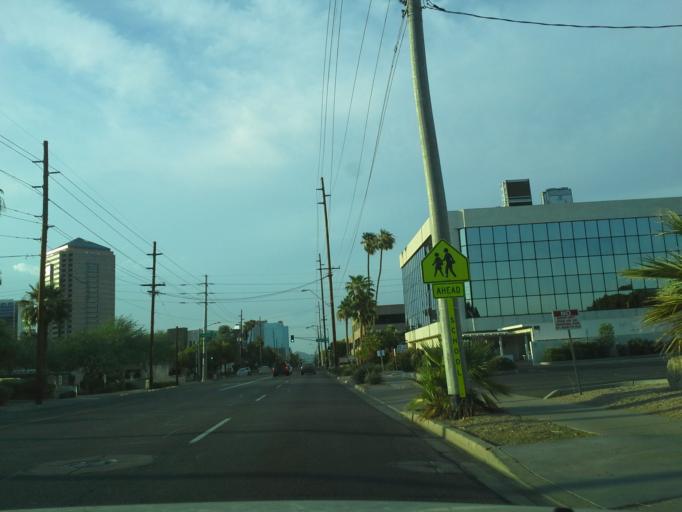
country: US
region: Arizona
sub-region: Maricopa County
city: Phoenix
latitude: 33.4755
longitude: -112.0694
